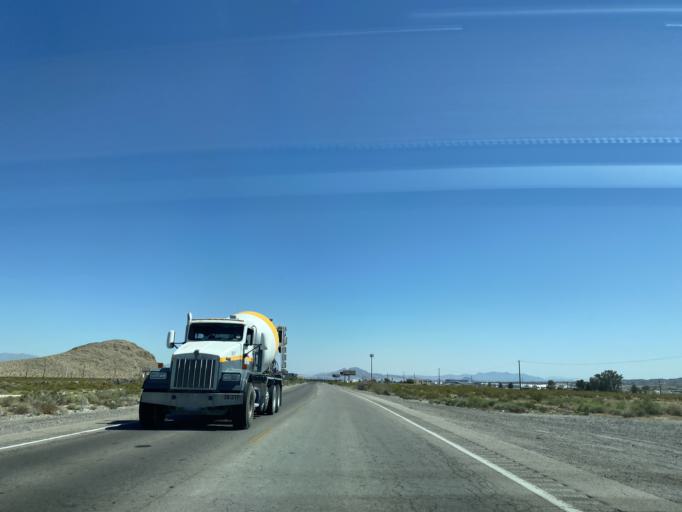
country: US
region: Nevada
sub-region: Clark County
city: Enterprise
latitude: 35.9439
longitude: -115.1810
